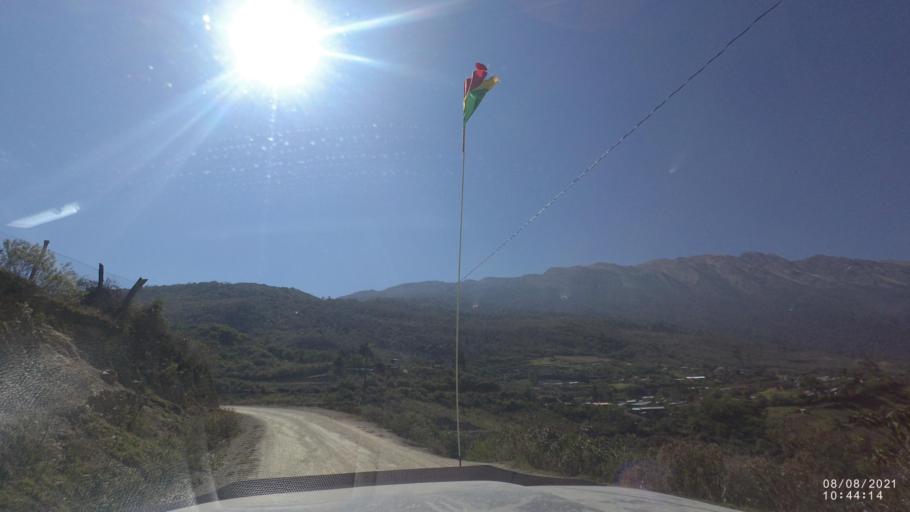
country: BO
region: La Paz
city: Quime
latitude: -16.7038
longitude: -66.7202
